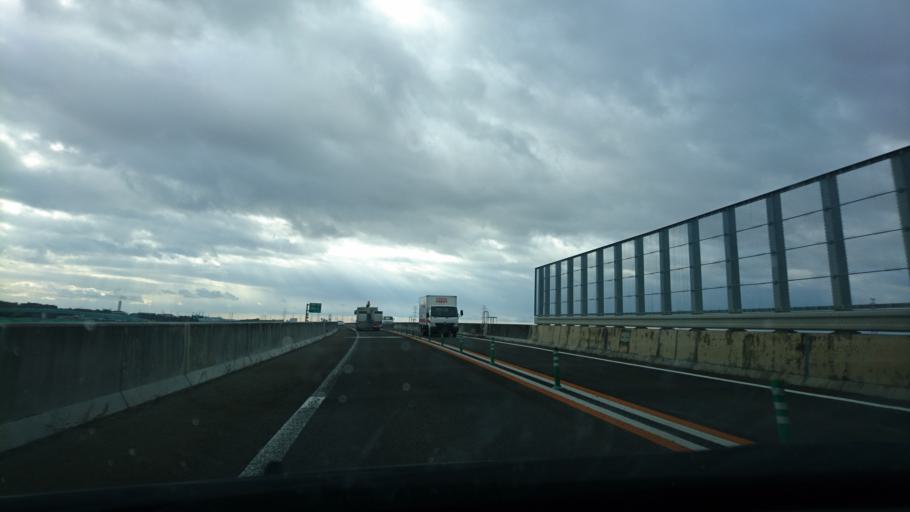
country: JP
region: Miyagi
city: Rifu
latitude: 38.3191
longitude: 140.9679
